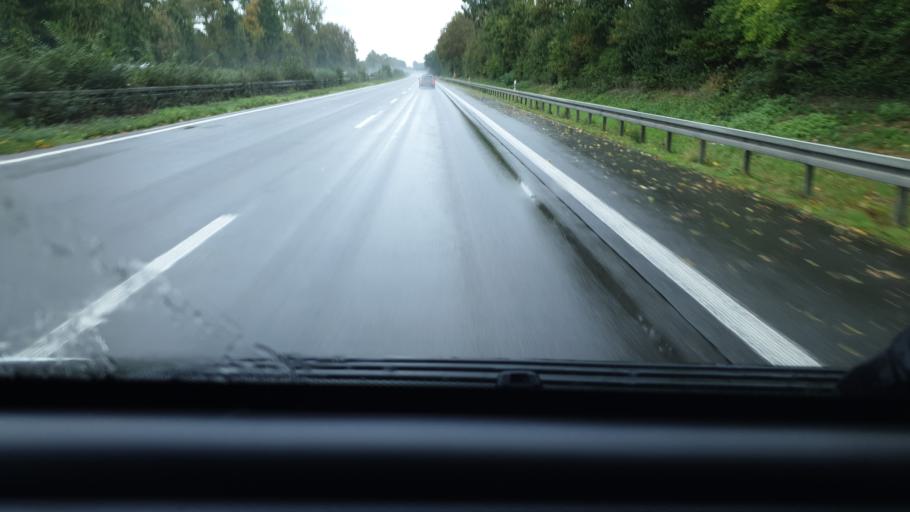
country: DE
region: North Rhine-Westphalia
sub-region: Regierungsbezirk Koln
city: Titz
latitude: 50.9798
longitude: 6.3772
